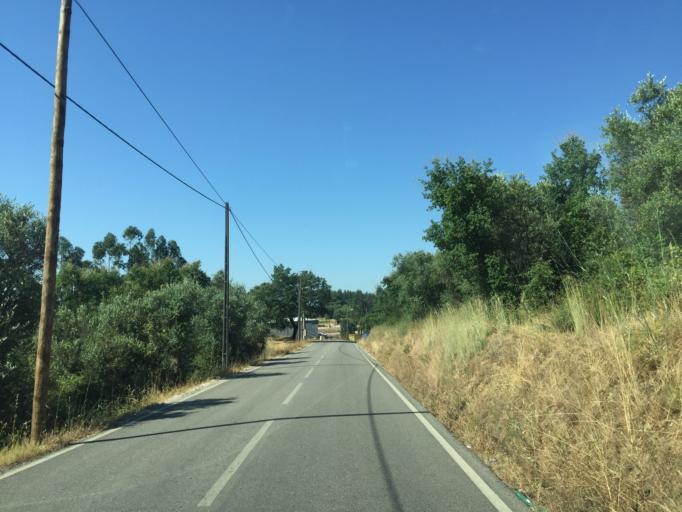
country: PT
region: Santarem
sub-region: Tomar
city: Tomar
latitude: 39.6006
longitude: -8.3136
